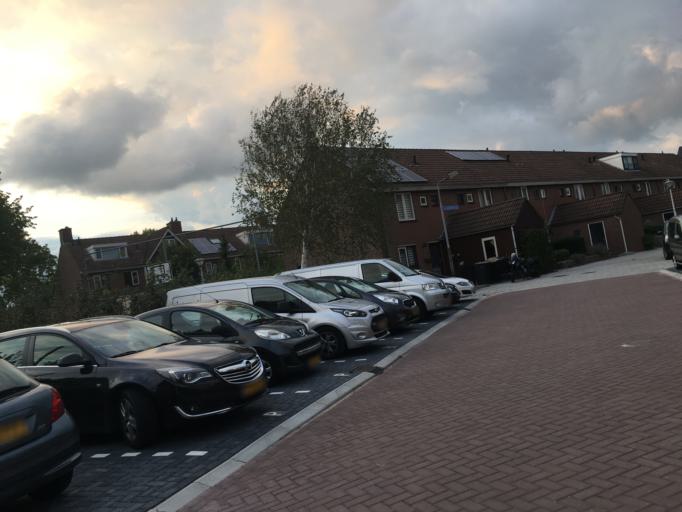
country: NL
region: North Holland
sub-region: Gemeente Zaanstad
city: Zaanstad
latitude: 52.4615
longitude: 4.7653
